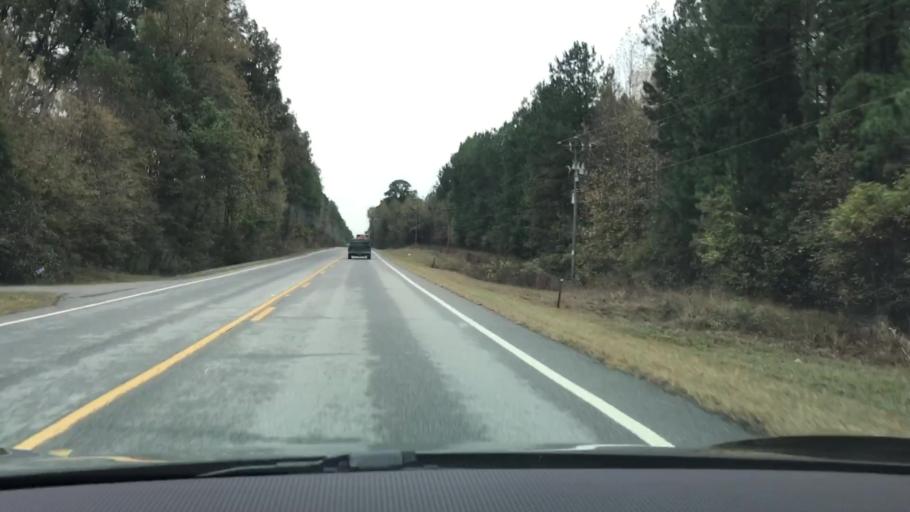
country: US
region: Georgia
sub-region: Greene County
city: Greensboro
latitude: 33.6313
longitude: -83.2159
